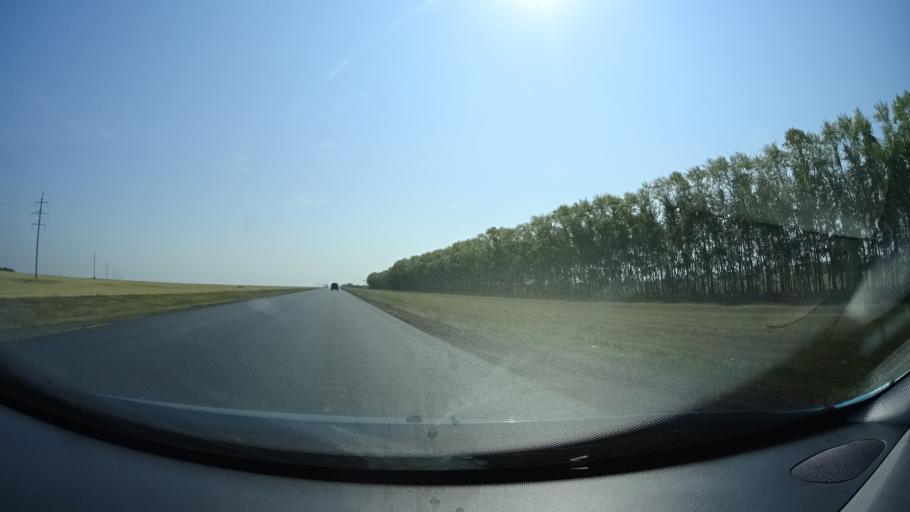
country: RU
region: Bashkortostan
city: Kabakovo
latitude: 54.4335
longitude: 56.0142
